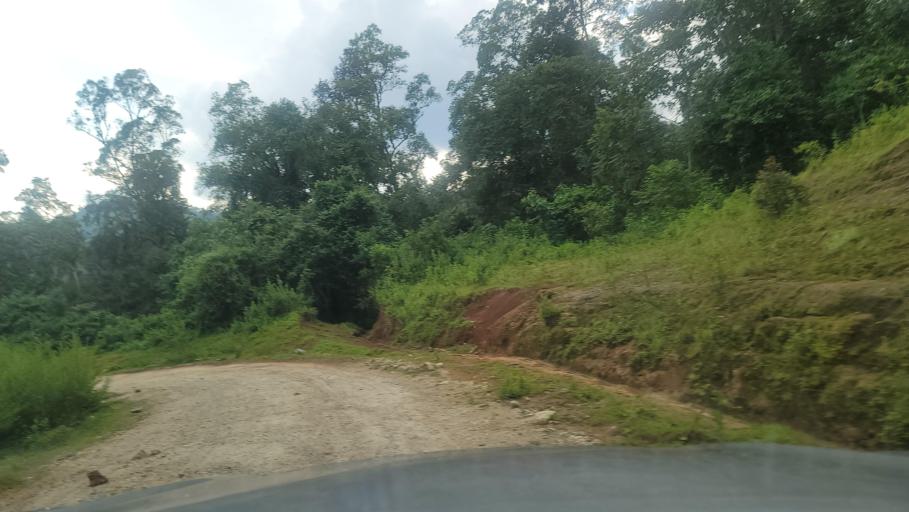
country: ET
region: Southern Nations, Nationalities, and People's Region
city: Bonga
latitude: 7.6219
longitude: 36.2095
